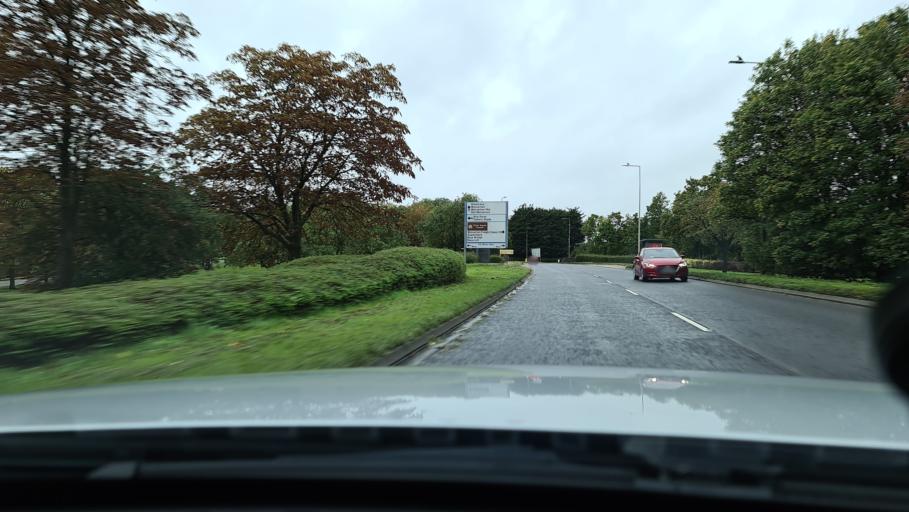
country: GB
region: England
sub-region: Milton Keynes
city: Bradwell
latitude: 52.0518
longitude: -0.8092
